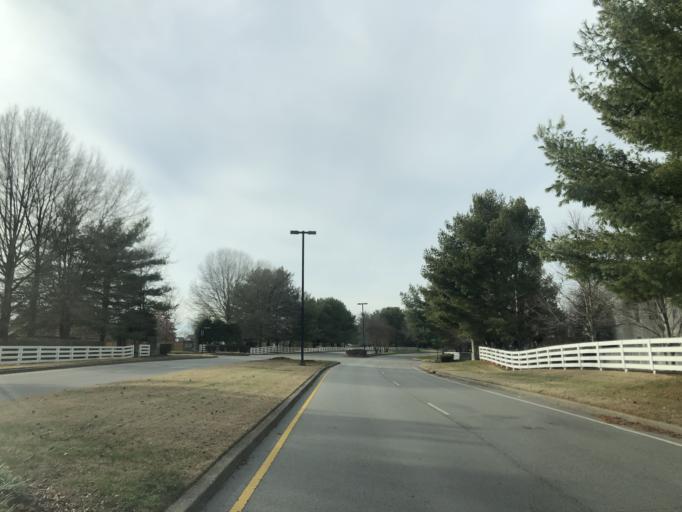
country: US
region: Tennessee
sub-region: Williamson County
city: Franklin
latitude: 35.9642
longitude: -86.8901
